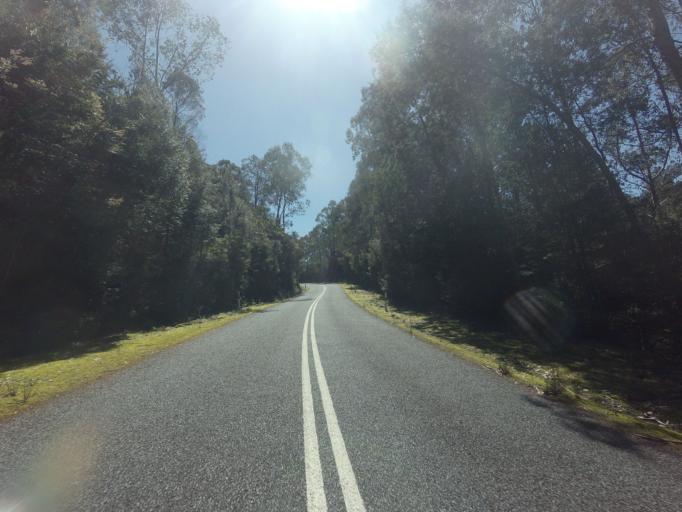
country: AU
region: Tasmania
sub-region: Huon Valley
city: Geeveston
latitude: -42.8147
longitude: 146.3739
